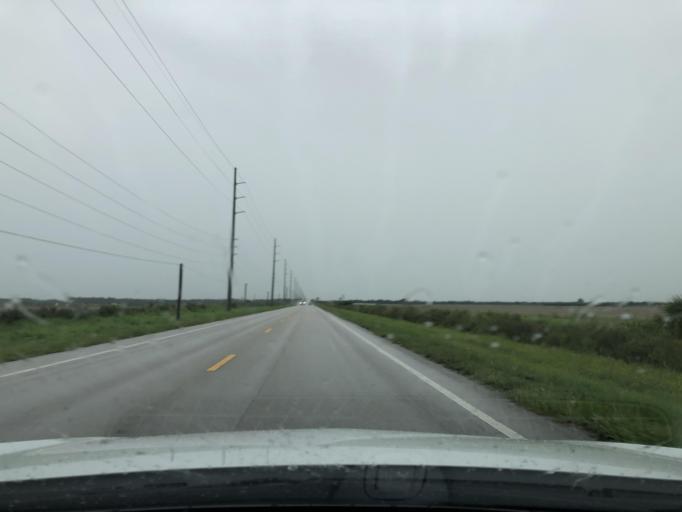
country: US
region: Florida
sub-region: Collier County
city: Orangetree
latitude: 26.2937
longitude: -81.4988
